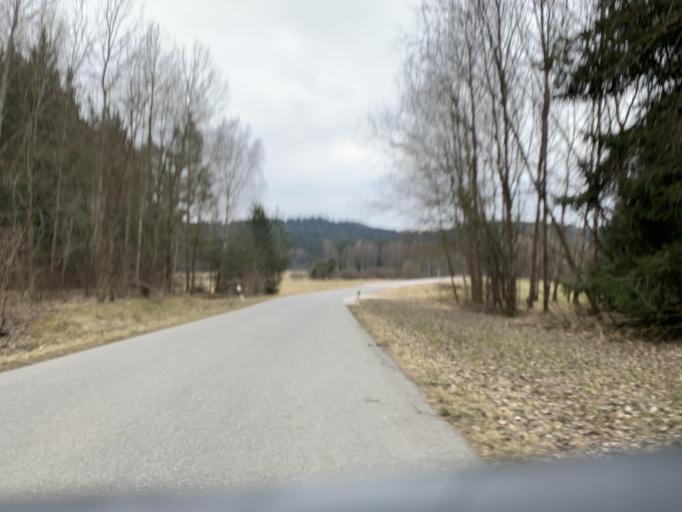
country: DE
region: Bavaria
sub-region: Upper Palatinate
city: Thanstein
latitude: 49.3947
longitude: 12.4577
